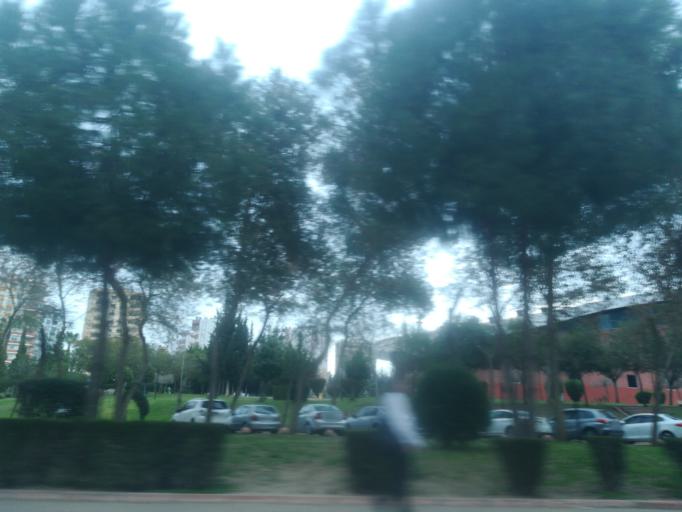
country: TR
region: Adana
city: Adana
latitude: 37.0367
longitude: 35.2943
